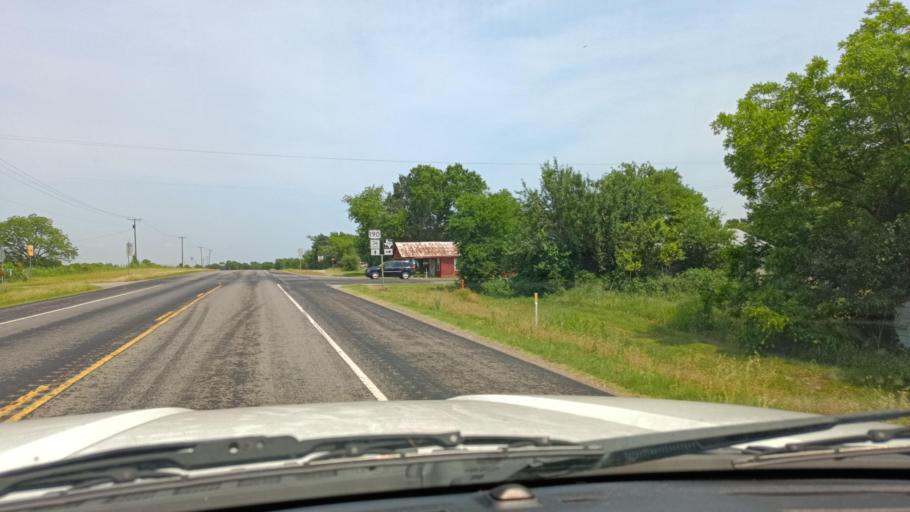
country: US
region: Texas
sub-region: Milam County
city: Cameron
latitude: 30.8502
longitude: -97.0817
